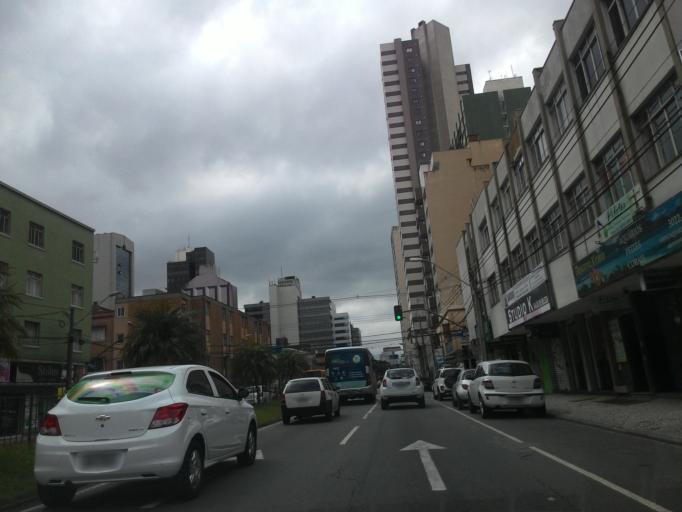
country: BR
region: Parana
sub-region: Curitiba
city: Curitiba
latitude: -25.4311
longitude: -49.2622
